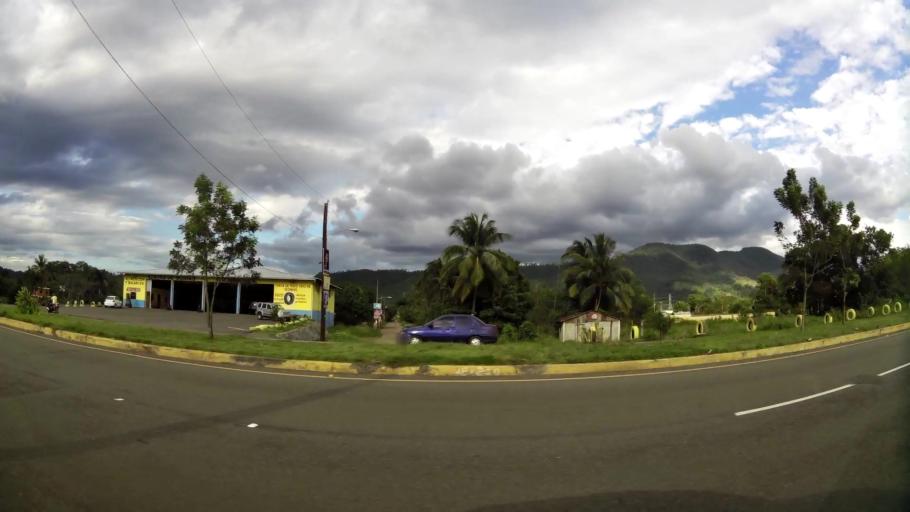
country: DO
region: Monsenor Nouel
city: Bonao
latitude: 18.9021
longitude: -70.3718
